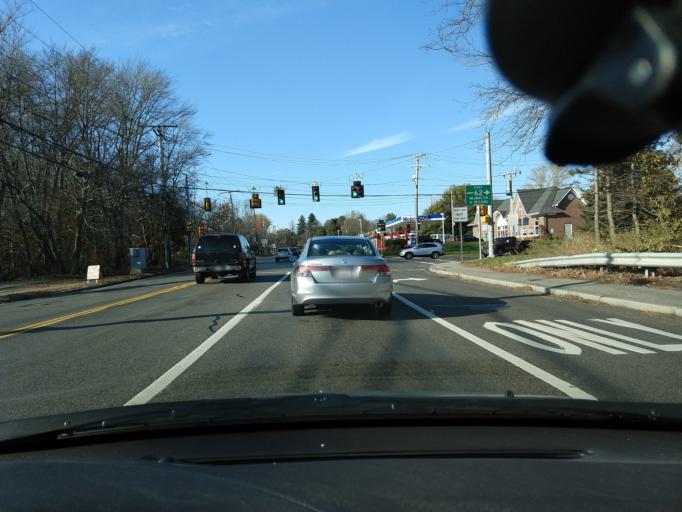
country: US
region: Massachusetts
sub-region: Middlesex County
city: Burlington
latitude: 42.5183
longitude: -71.2098
